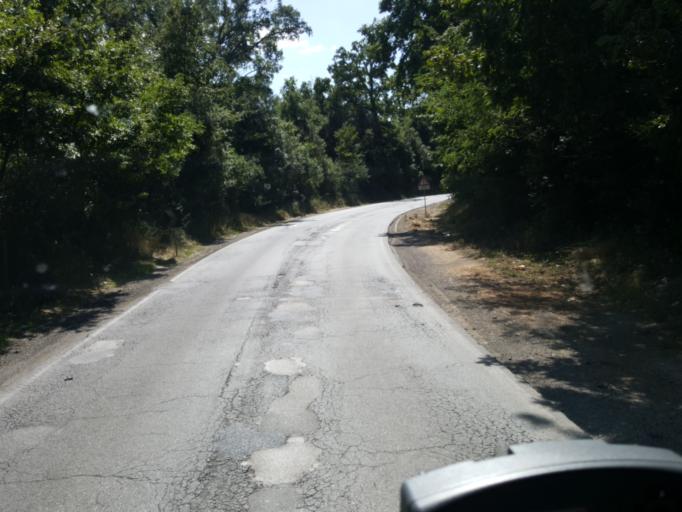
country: IT
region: Latium
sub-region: Provincia di Latina
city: Roccasecca dei Volsci
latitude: 41.4516
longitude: 13.2026
